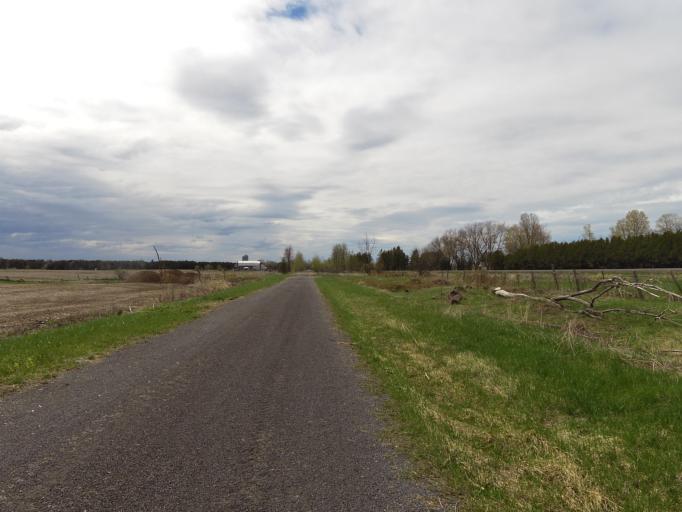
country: CA
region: Ontario
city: Hawkesbury
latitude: 45.5409
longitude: -74.7468
